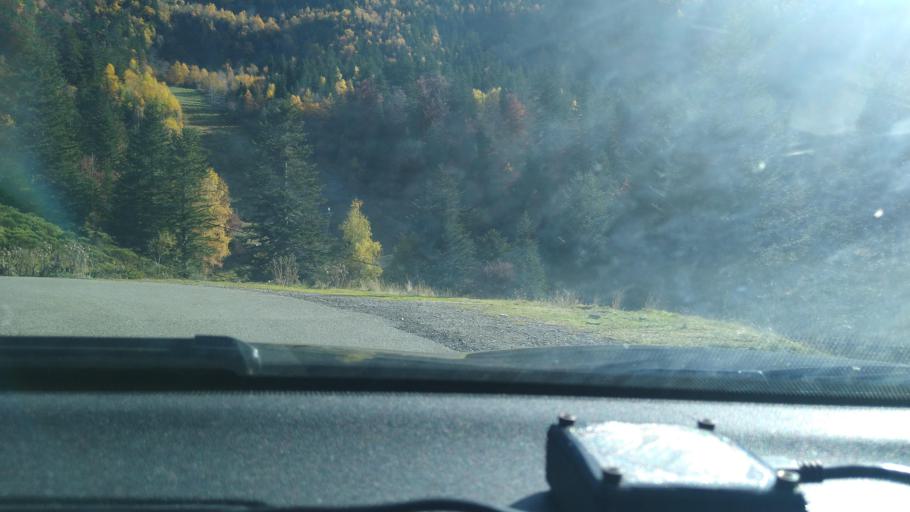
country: FR
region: Midi-Pyrenees
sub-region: Departement de l'Ariege
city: Ax-les-Thermes
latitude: 42.7274
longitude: 1.9619
